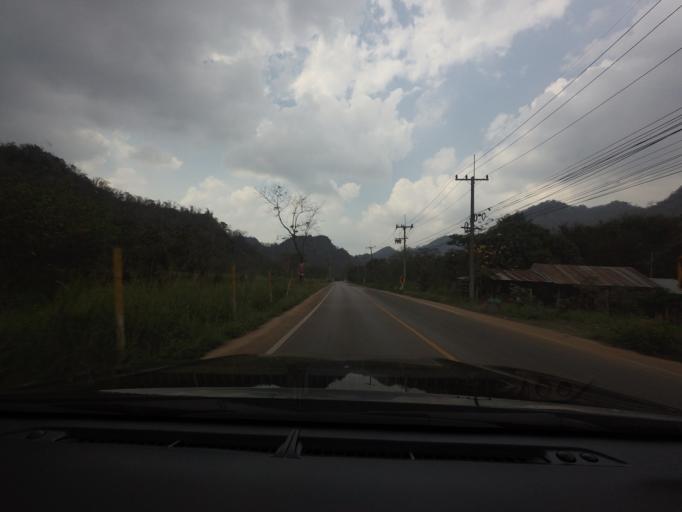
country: TH
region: Sara Buri
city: Muak Lek
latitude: 14.5700
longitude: 101.2925
